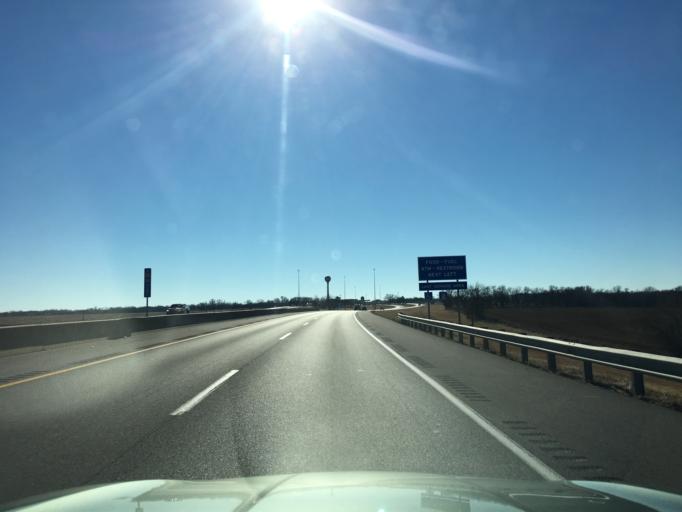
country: US
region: Kansas
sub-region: Sumner County
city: Belle Plaine
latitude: 37.3740
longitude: -97.3231
